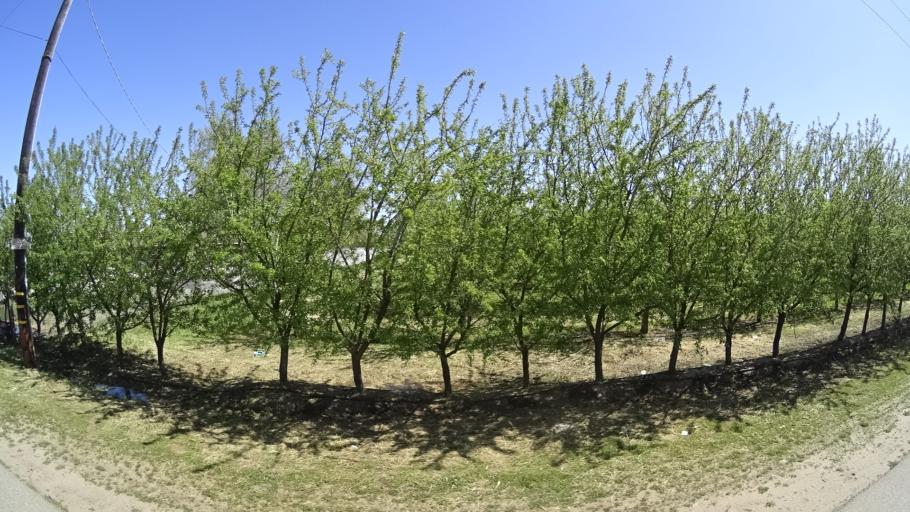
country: US
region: California
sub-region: Fresno County
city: West Park
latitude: 36.7148
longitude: -119.8445
